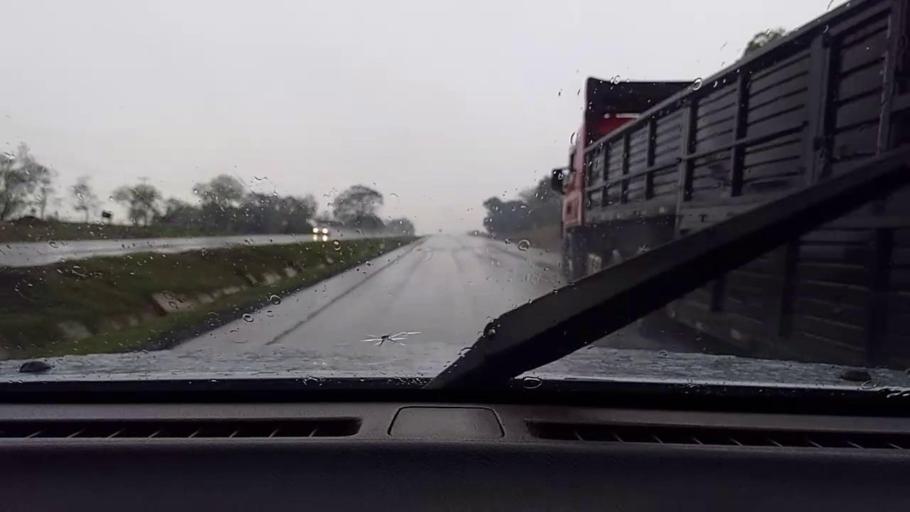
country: PY
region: Caaguazu
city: Repatriacion
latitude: -25.4452
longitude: -55.8834
